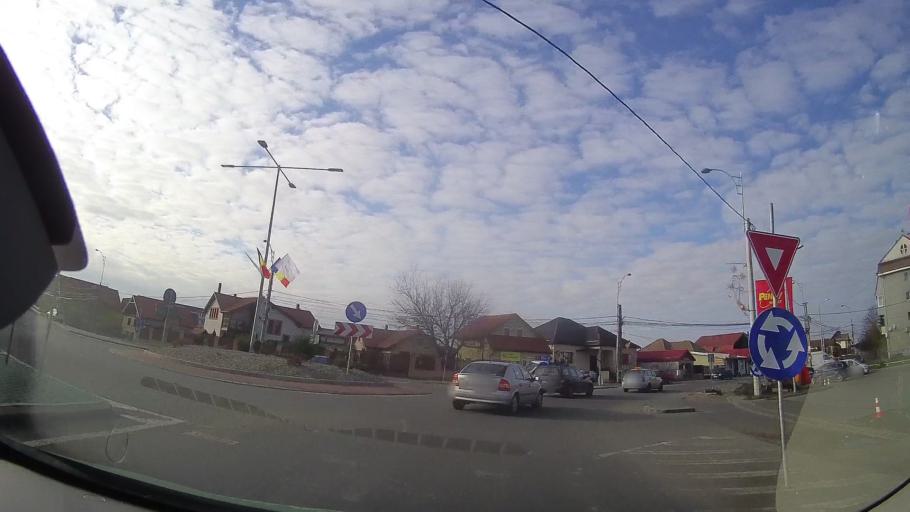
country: RO
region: Cluj
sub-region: Comuna Apahida
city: Apahida
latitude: 46.7999
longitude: 23.7548
